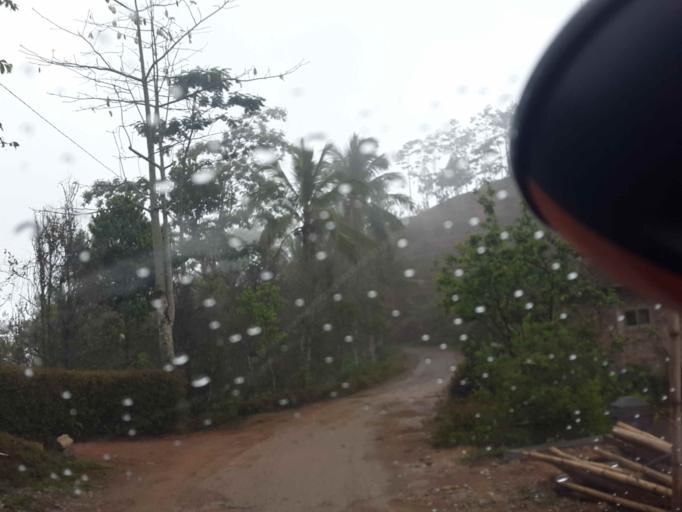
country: ID
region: East Java
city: Krajan Mrayan
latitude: -8.1185
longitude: 111.3400
